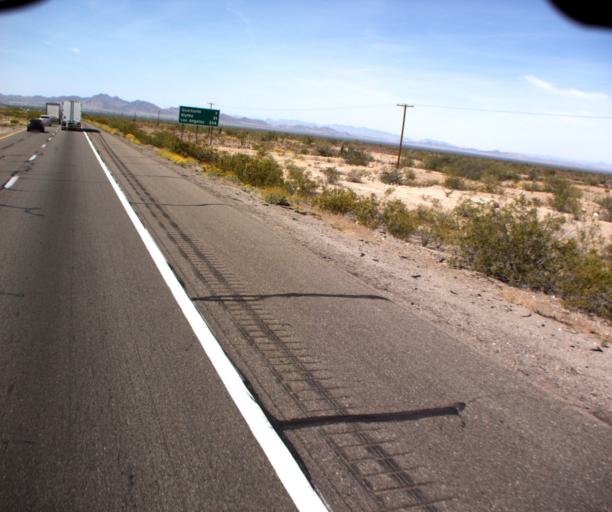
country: US
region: Arizona
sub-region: La Paz County
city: Quartzsite
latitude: 33.6792
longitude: -114.0980
